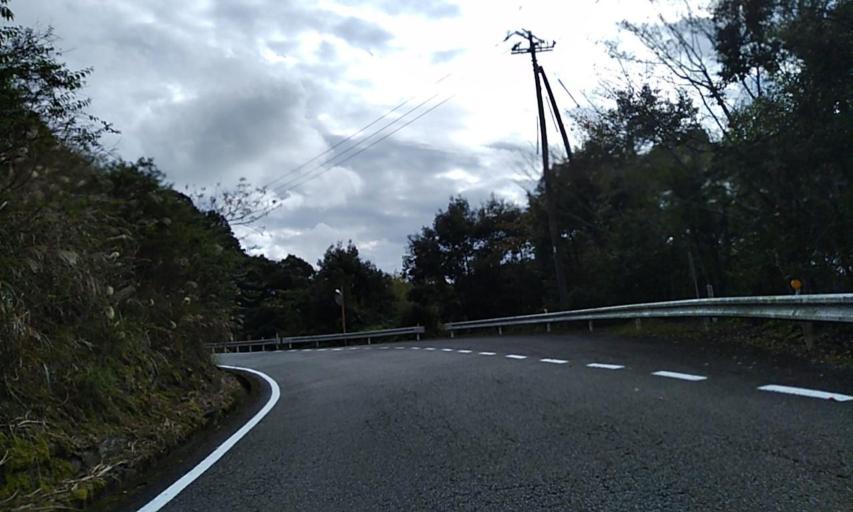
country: JP
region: Wakayama
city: Shingu
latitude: 33.5427
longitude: 135.8351
